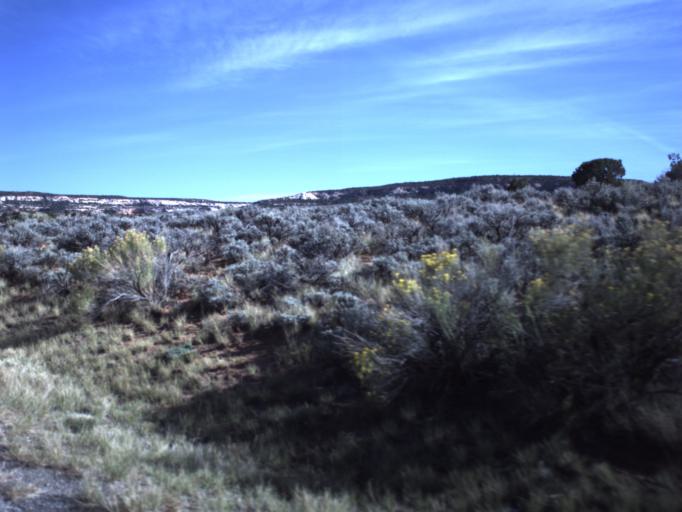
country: US
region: Utah
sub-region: Grand County
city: Moab
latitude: 38.3075
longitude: -109.3978
